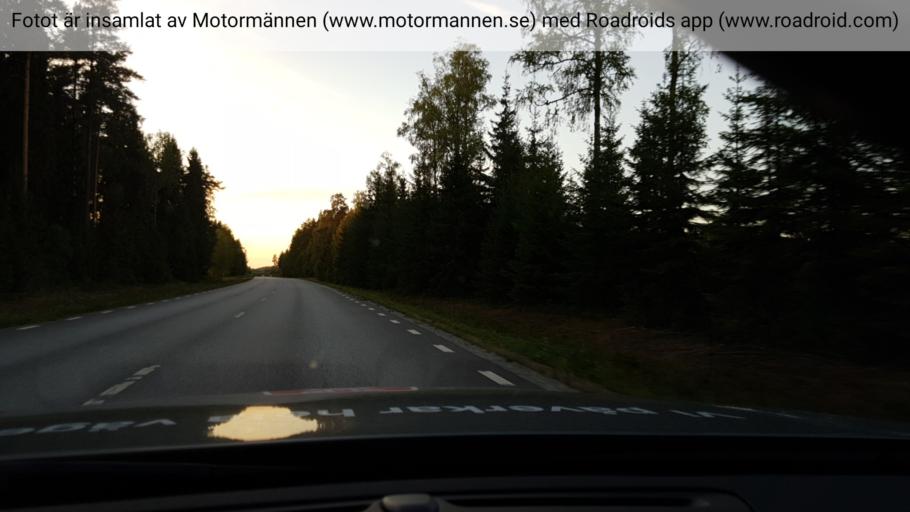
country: SE
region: OErebro
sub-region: Karlskoga Kommun
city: Karlskoga
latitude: 59.4156
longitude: 14.5170
